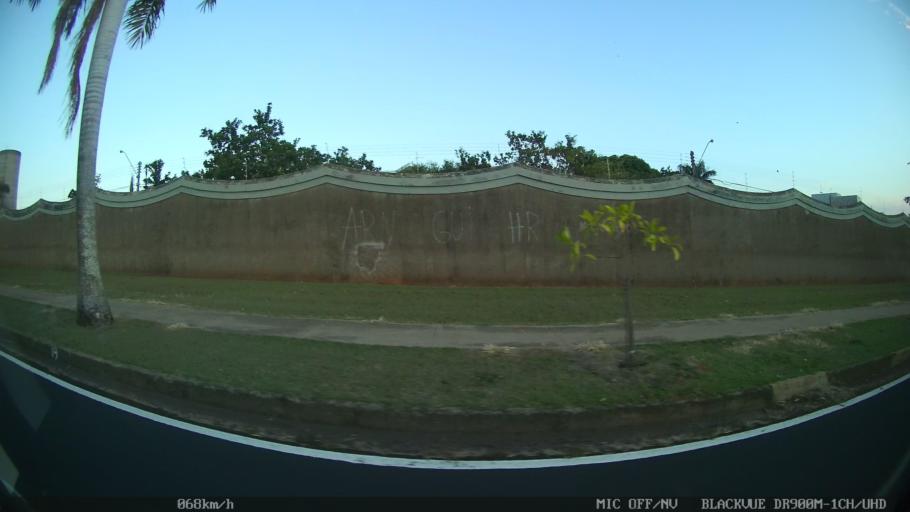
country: BR
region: Sao Paulo
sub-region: Sao Jose Do Rio Preto
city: Sao Jose do Rio Preto
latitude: -20.8171
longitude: -49.3407
